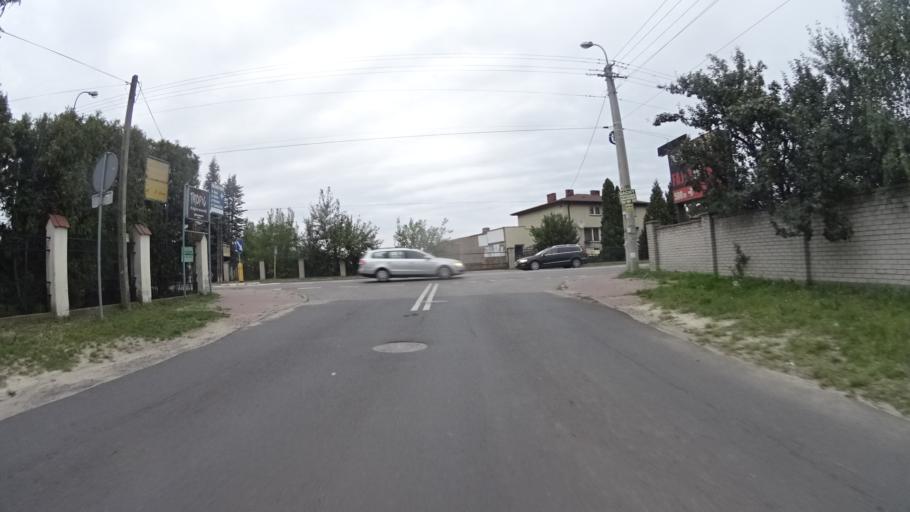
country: PL
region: Masovian Voivodeship
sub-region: Powiat warszawski zachodni
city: Hornowek
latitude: 52.2543
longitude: 20.7915
